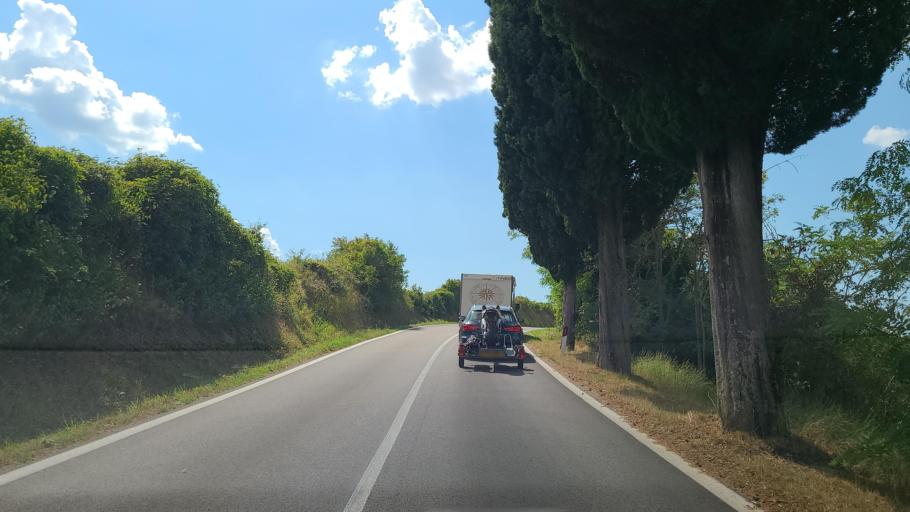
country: IT
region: Tuscany
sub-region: Provincia di Siena
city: San Gimignano
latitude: 43.4046
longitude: 11.0128
